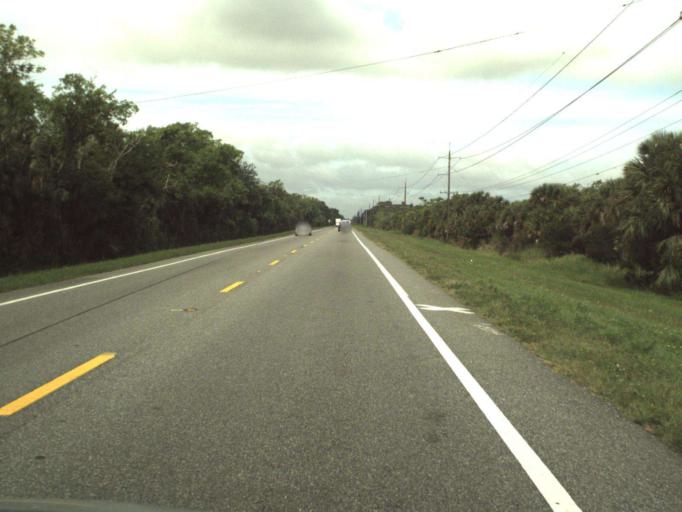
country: US
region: Florida
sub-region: Seminole County
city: Midway
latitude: 28.7869
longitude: -81.1936
